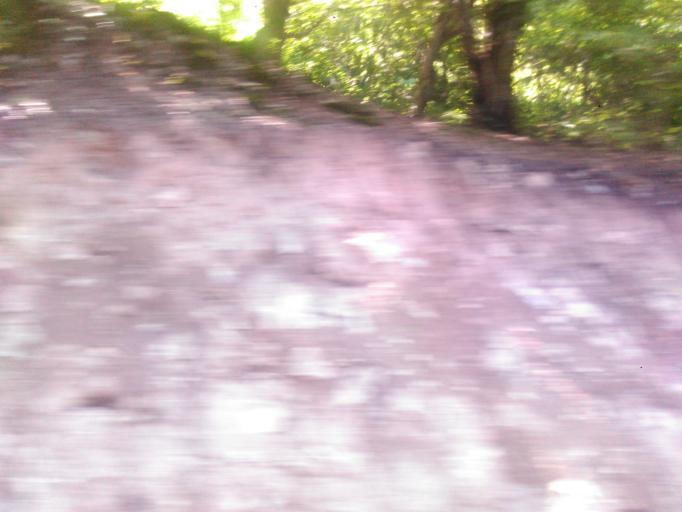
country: GE
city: Zhinvali
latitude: 42.1786
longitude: 44.8109
